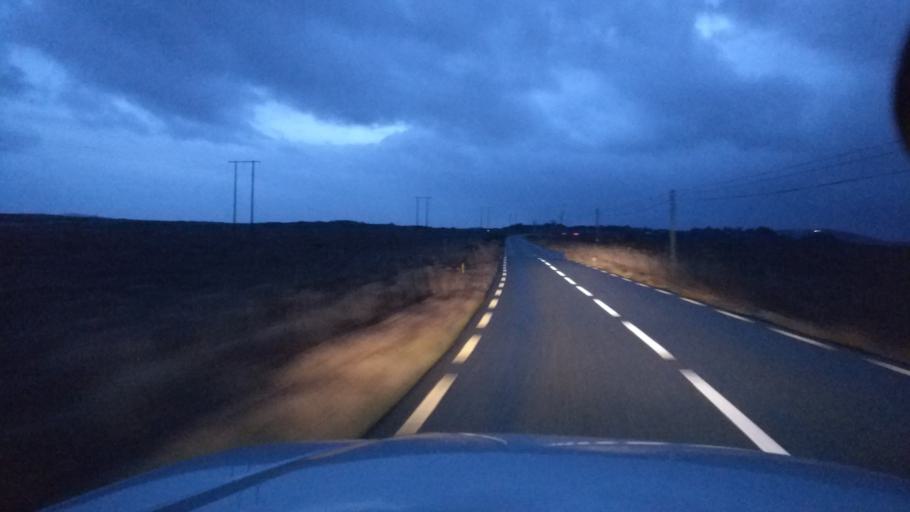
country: IE
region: Connaught
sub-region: County Galway
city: Oughterard
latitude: 53.4016
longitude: -9.5440
